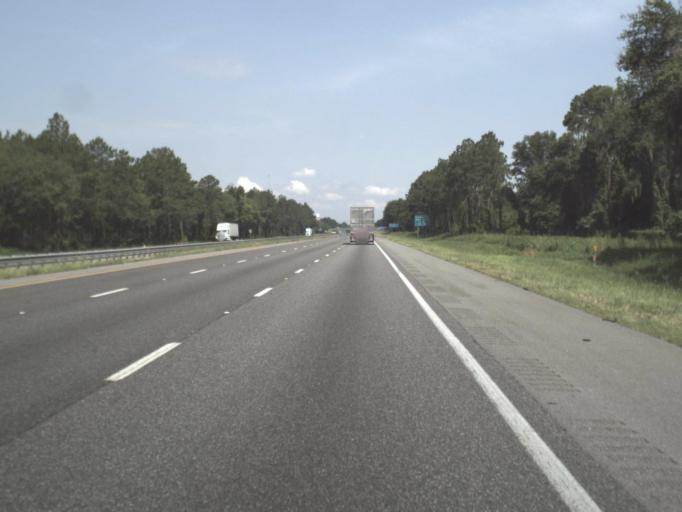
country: US
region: Florida
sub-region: Hamilton County
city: Jasper
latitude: 30.4421
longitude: -82.9219
